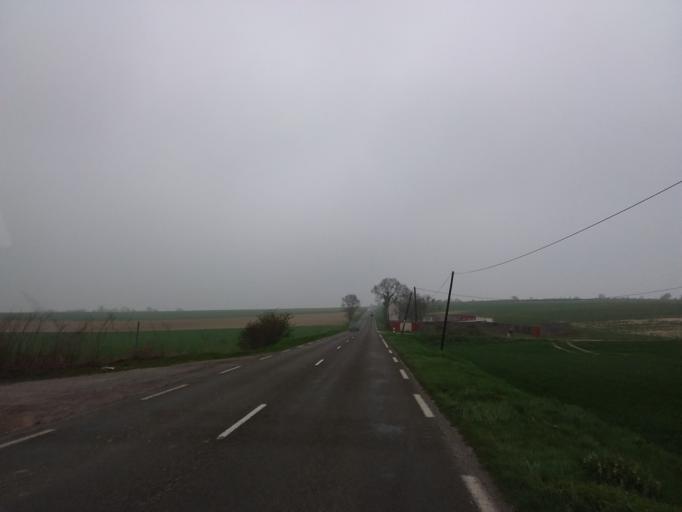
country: FR
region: Picardie
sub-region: Departement de l'Aisne
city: Omissy
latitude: 49.8741
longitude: 3.3001
